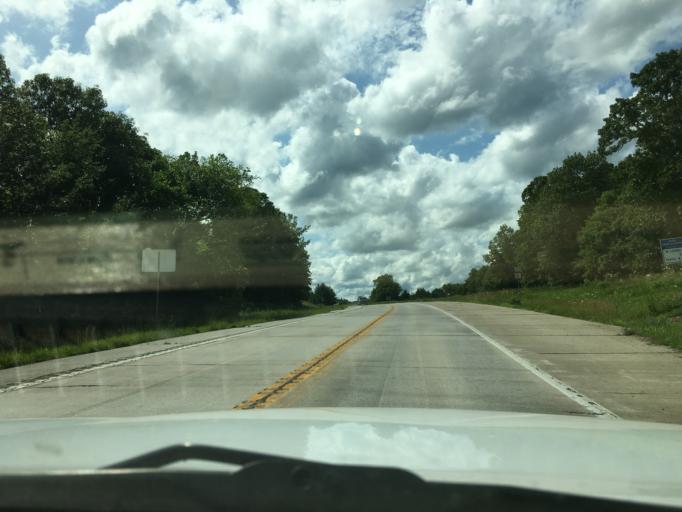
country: US
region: Missouri
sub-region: Franklin County
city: Gerald
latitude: 38.4223
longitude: -91.2595
